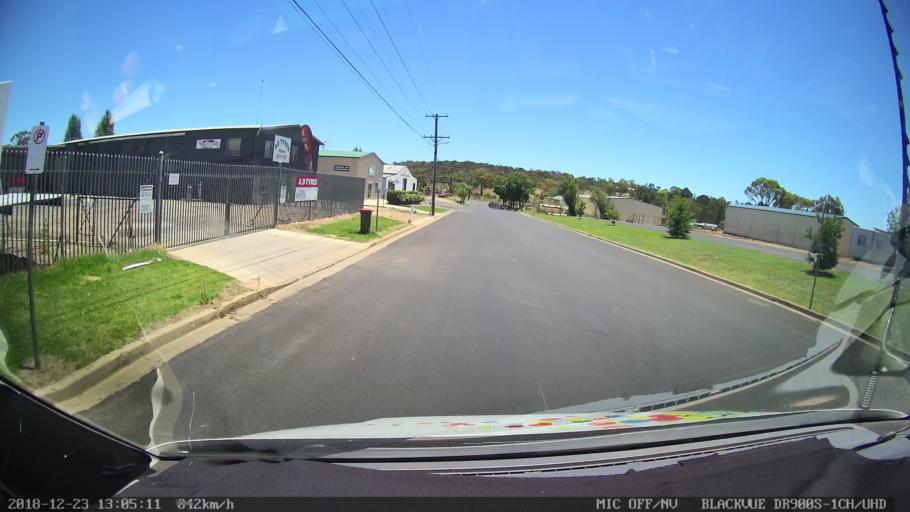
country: AU
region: New South Wales
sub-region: Armidale Dumaresq
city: Armidale
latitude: -30.5147
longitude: 151.6435
